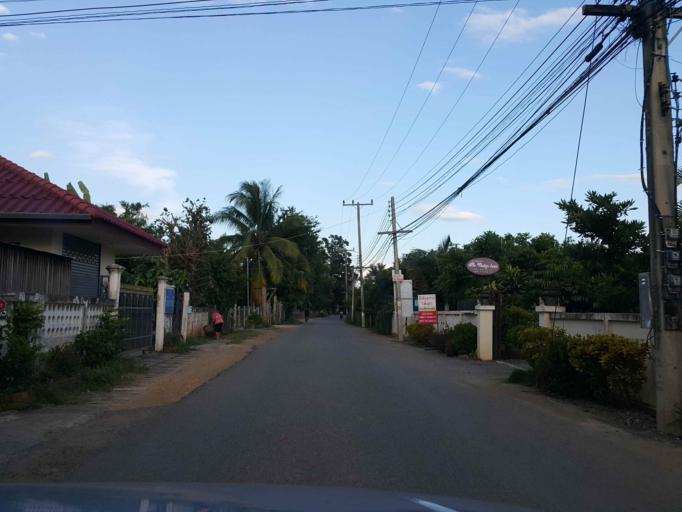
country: TH
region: Chiang Mai
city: San Sai
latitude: 18.8992
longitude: 98.9835
